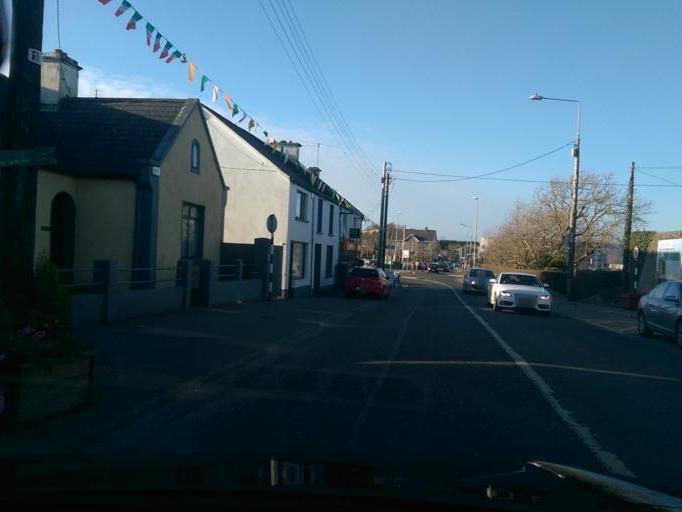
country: IE
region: Connaught
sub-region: County Galway
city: Oranmore
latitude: 53.2706
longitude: -8.9289
